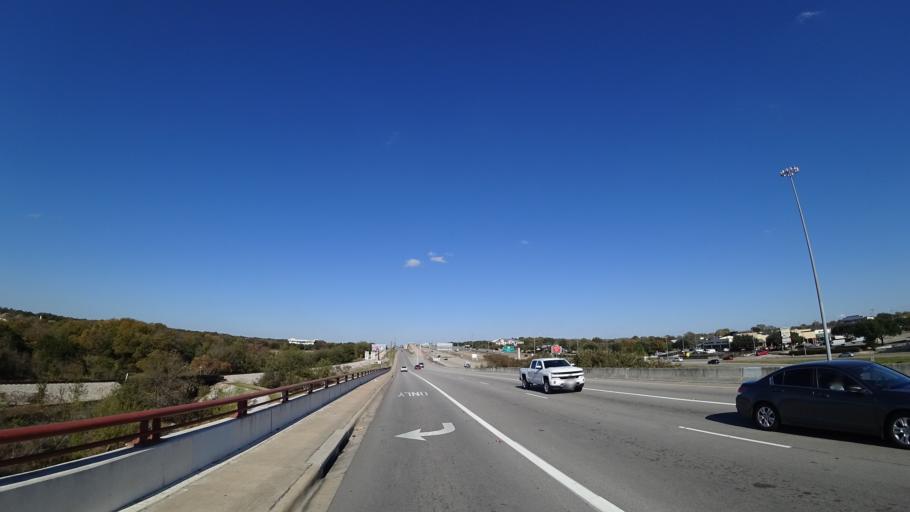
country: US
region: Texas
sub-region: Travis County
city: Wells Branch
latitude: 30.4211
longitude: -97.7045
